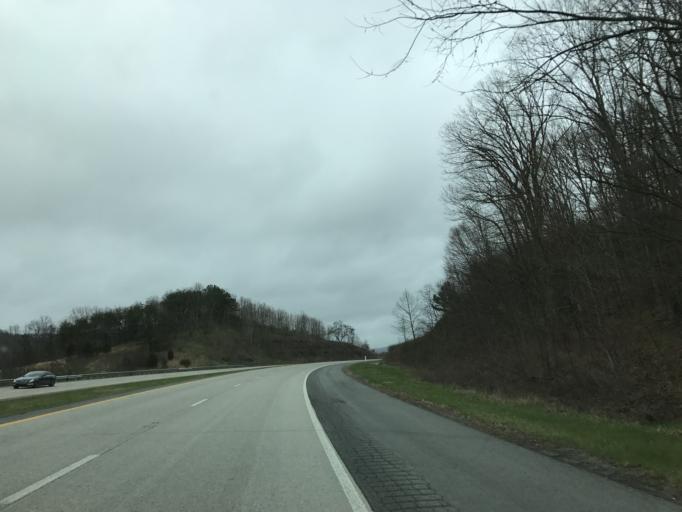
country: US
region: West Virginia
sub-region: Summers County
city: Hinton
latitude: 37.7912
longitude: -80.8731
